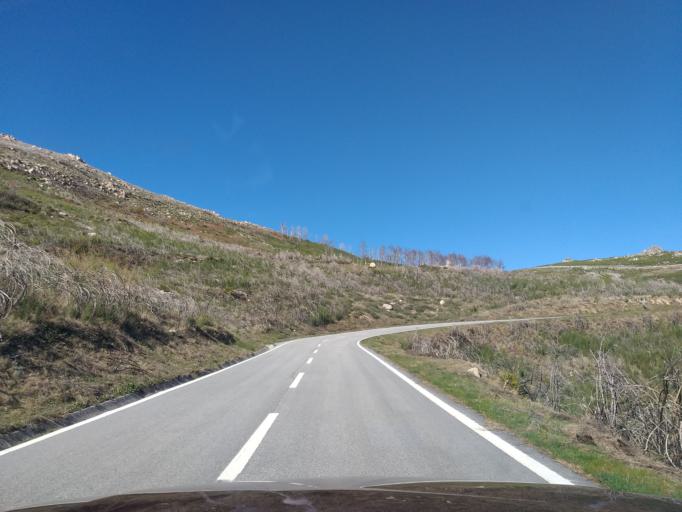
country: PT
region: Guarda
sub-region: Manteigas
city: Manteigas
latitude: 40.4764
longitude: -7.5159
